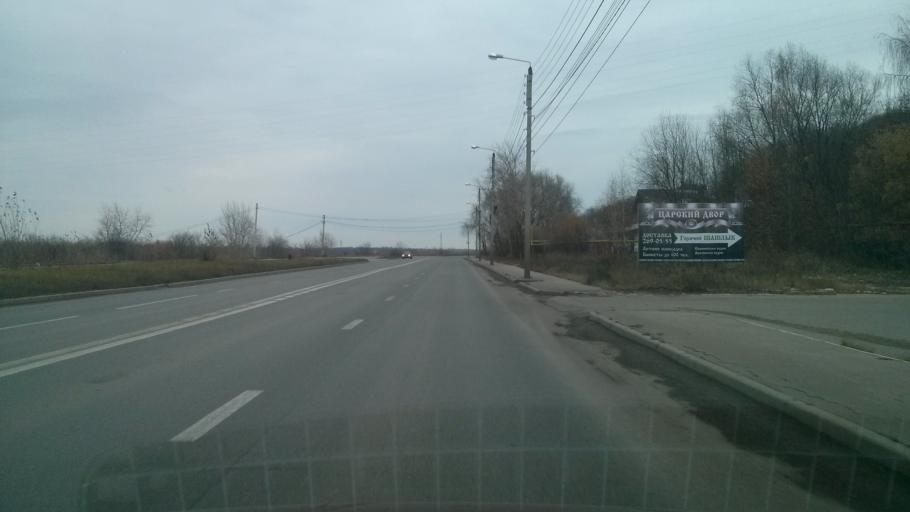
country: RU
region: Nizjnij Novgorod
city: Bor
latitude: 56.3180
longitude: 44.0771
